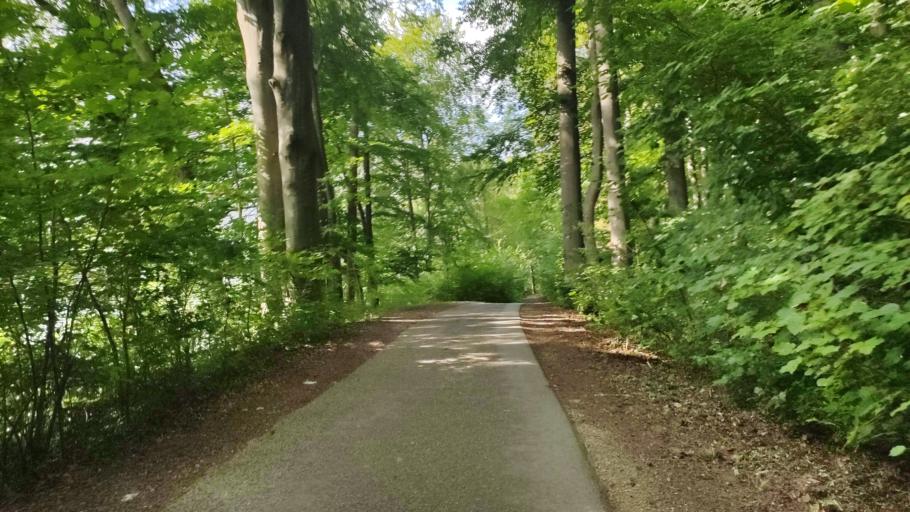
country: DE
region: Bavaria
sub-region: Upper Bavaria
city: Kaufering
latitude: 48.1059
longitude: 10.8705
